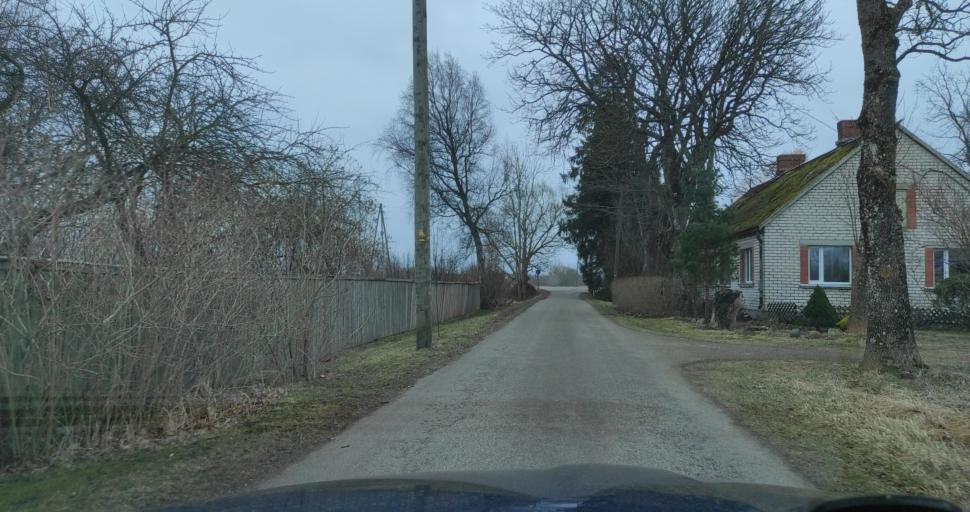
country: LV
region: Ventspils Rajons
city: Piltene
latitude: 57.2226
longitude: 21.6876
